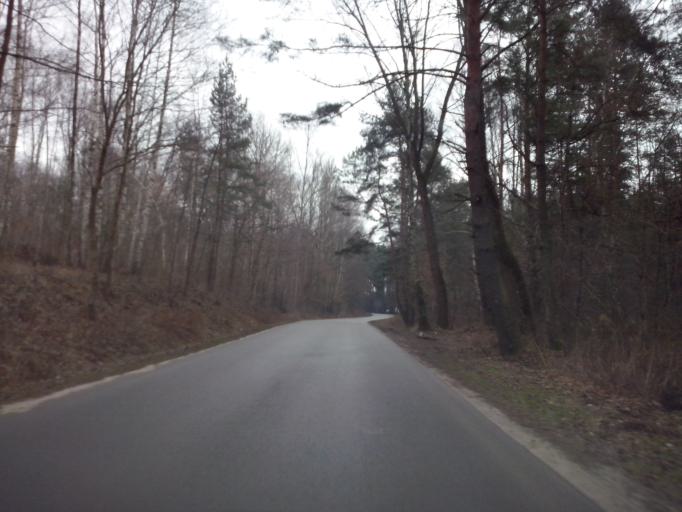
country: PL
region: Subcarpathian Voivodeship
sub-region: Powiat nizanski
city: Bieliny
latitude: 50.4330
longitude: 22.3061
